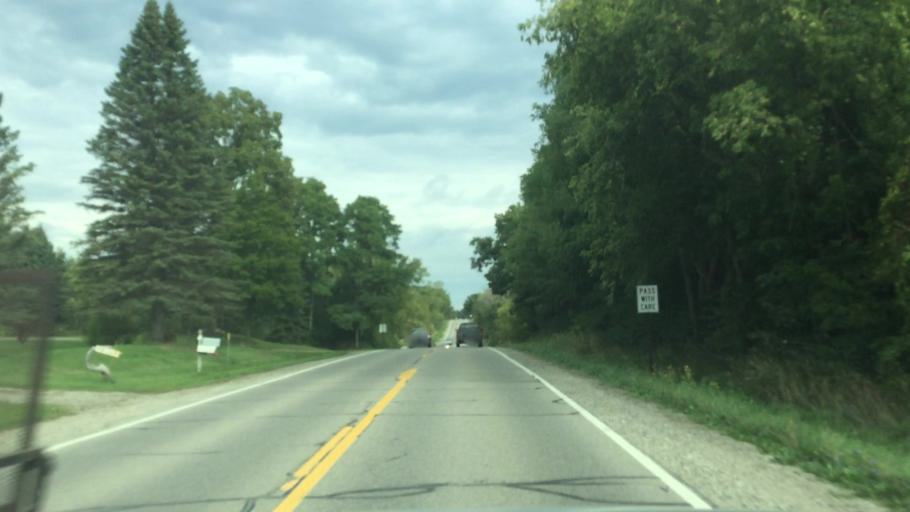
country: US
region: Michigan
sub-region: Livingston County
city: Howell
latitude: 42.6364
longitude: -83.8757
